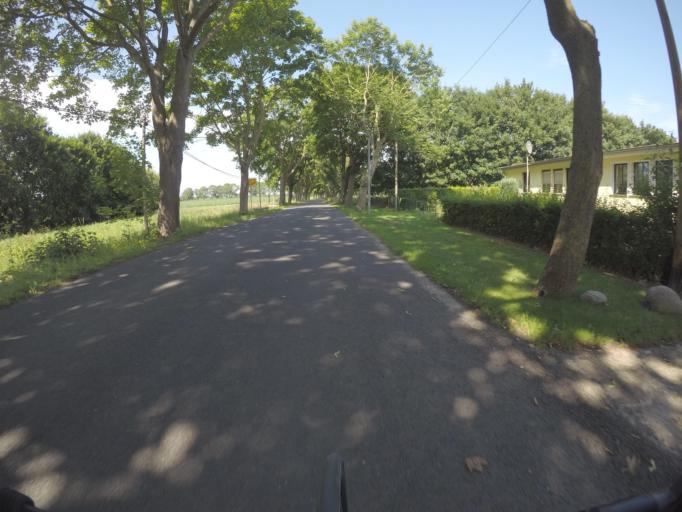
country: DE
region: Mecklenburg-Vorpommern
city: Gingst
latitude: 54.4390
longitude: 13.2233
